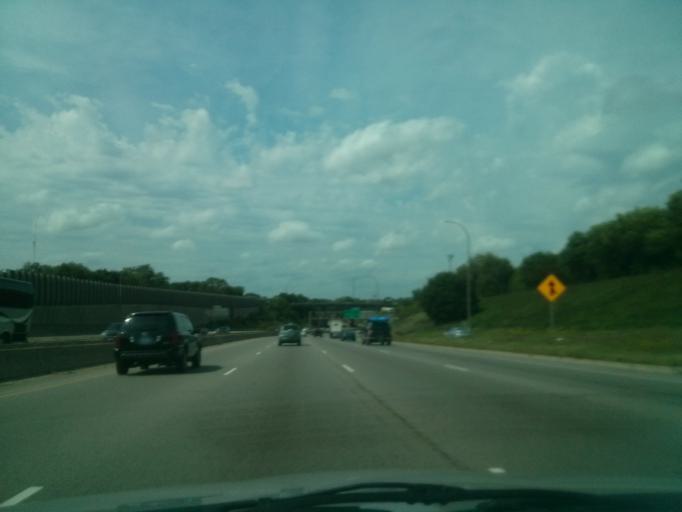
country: US
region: Minnesota
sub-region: Ramsey County
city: Lauderdale
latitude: 44.9573
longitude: -93.1957
